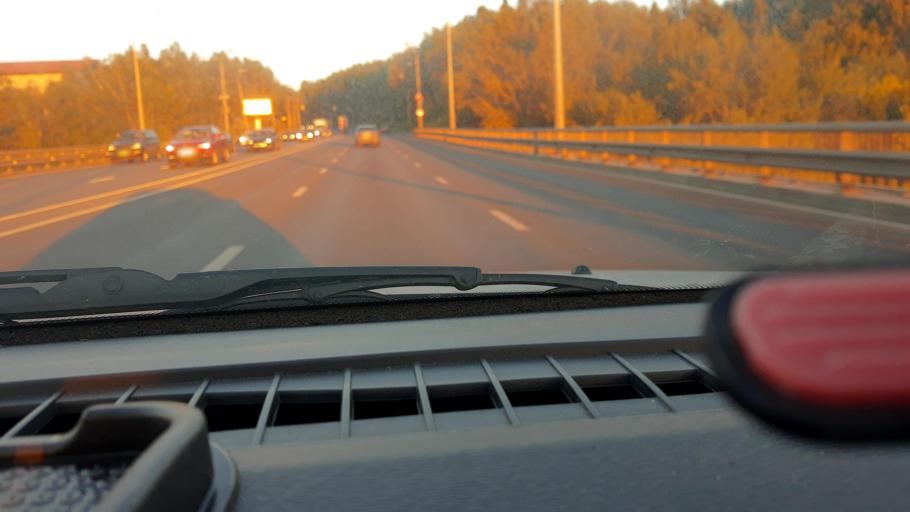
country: RU
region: Nizjnij Novgorod
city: Nizhniy Novgorod
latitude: 56.2495
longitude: 43.9568
